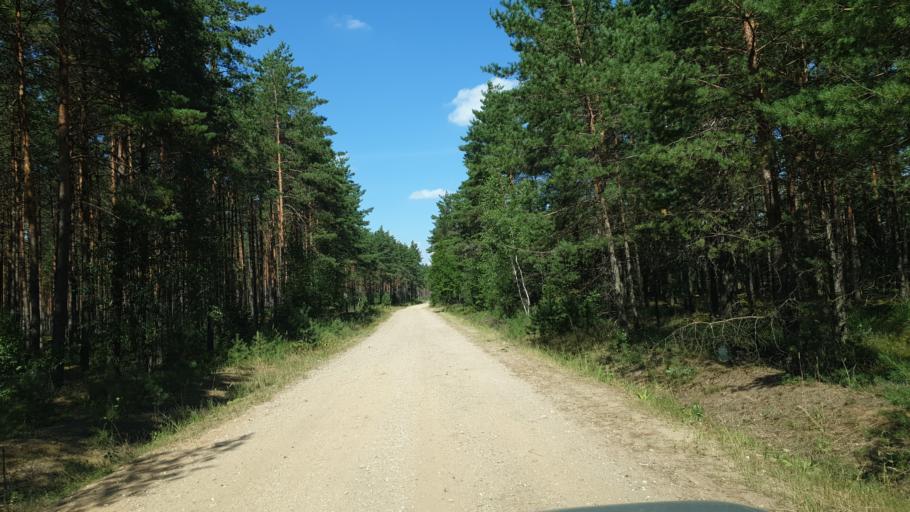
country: LT
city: Sirvintos
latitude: 54.8946
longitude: 24.9571
